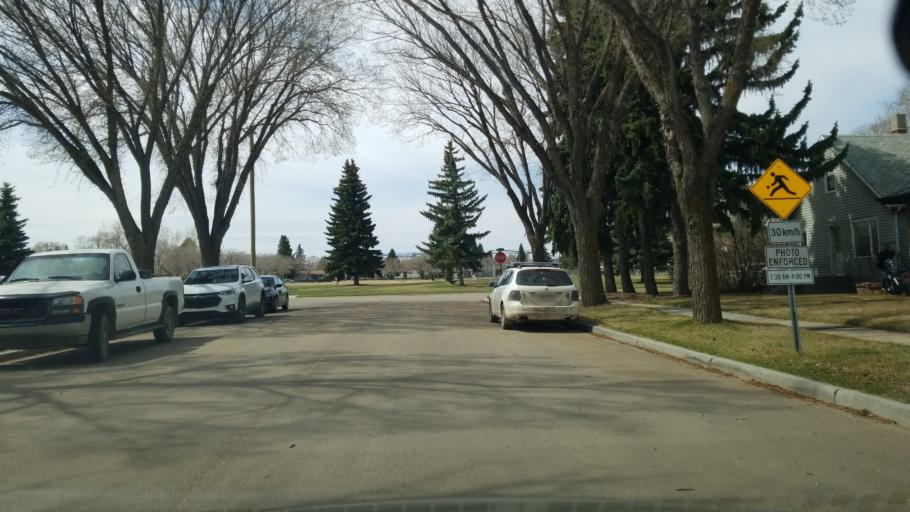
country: CA
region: Saskatchewan
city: Lloydminster
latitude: 53.2825
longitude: -110.0196
